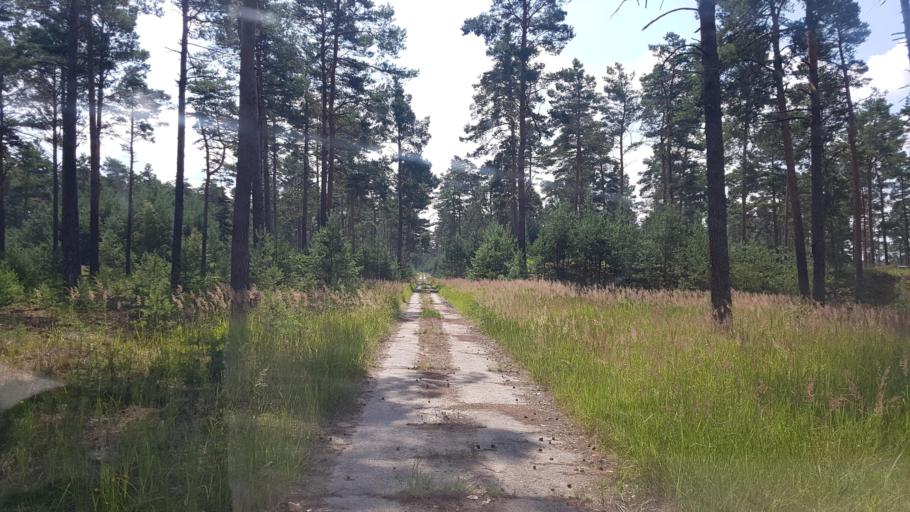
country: DE
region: Brandenburg
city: Crinitz
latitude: 51.7079
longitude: 13.7388
